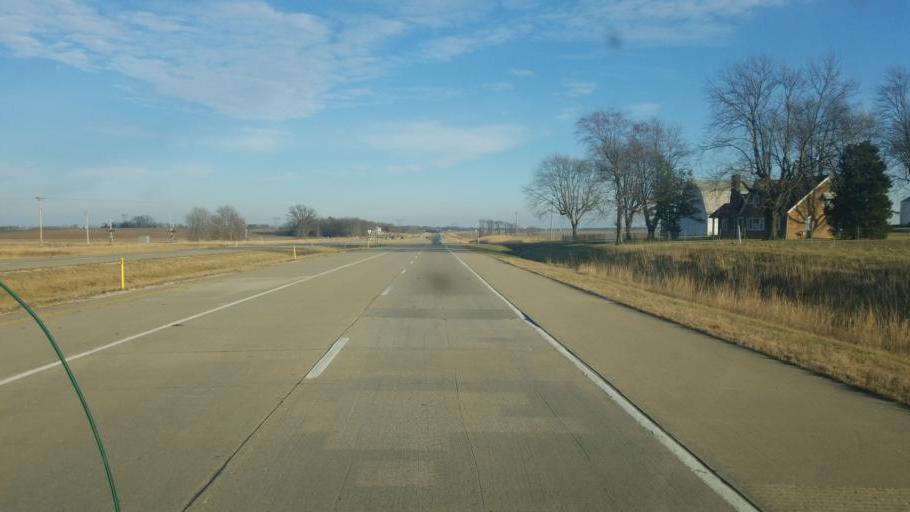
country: US
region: Indiana
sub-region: Knox County
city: Bicknell
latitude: 38.6730
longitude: -87.3586
